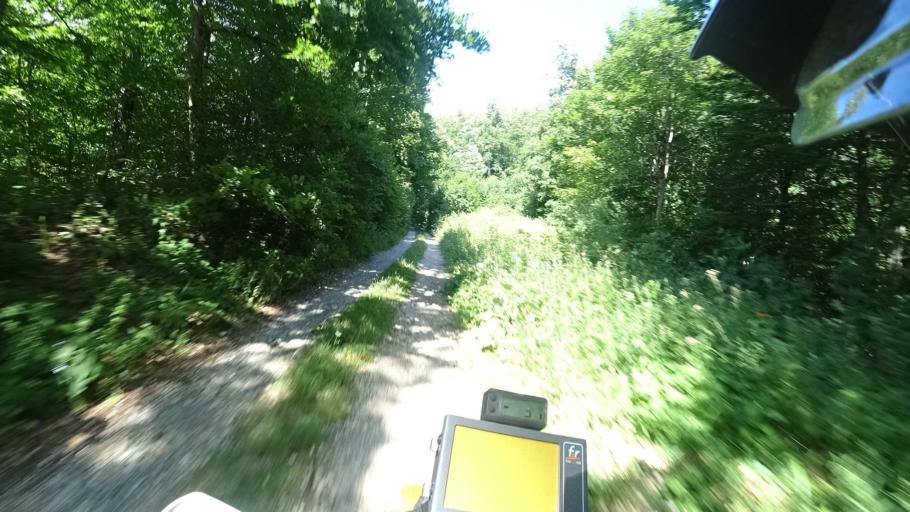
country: HR
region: Karlovacka
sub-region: Grad Ogulin
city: Ogulin
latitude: 45.1750
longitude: 15.1274
